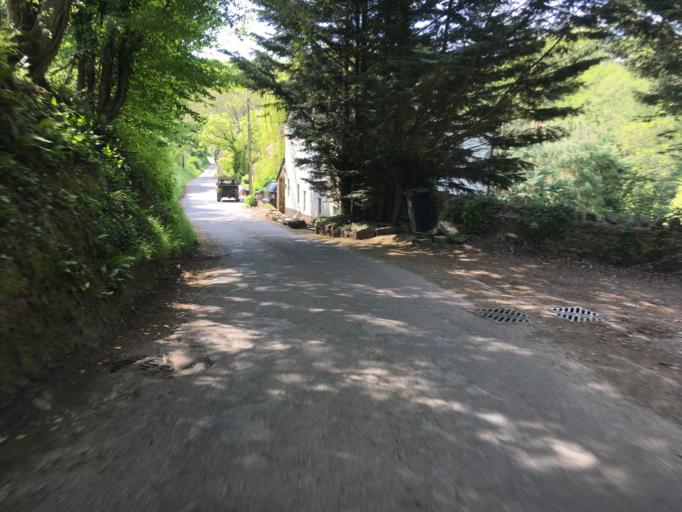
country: GB
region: England
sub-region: South Gloucestershire
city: Falfield
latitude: 51.6141
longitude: -2.4473
